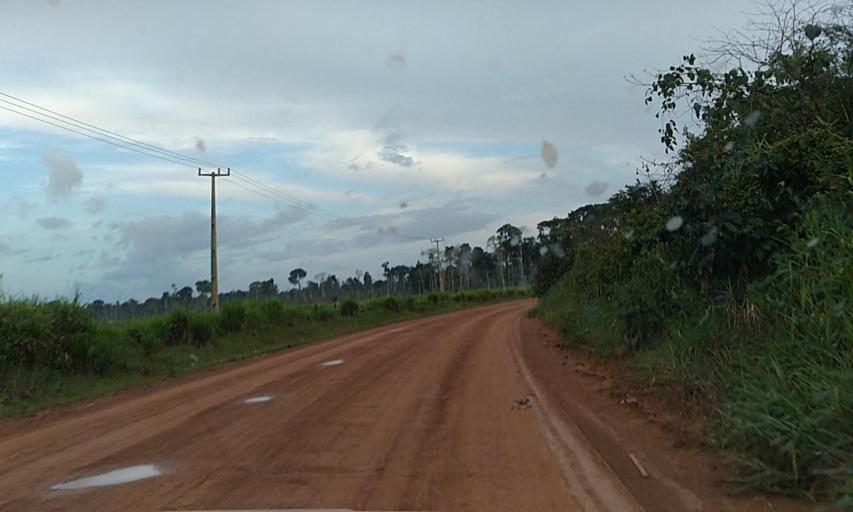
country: BR
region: Para
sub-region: Senador Jose Porfirio
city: Senador Jose Porfirio
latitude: -2.7044
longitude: -51.8133
